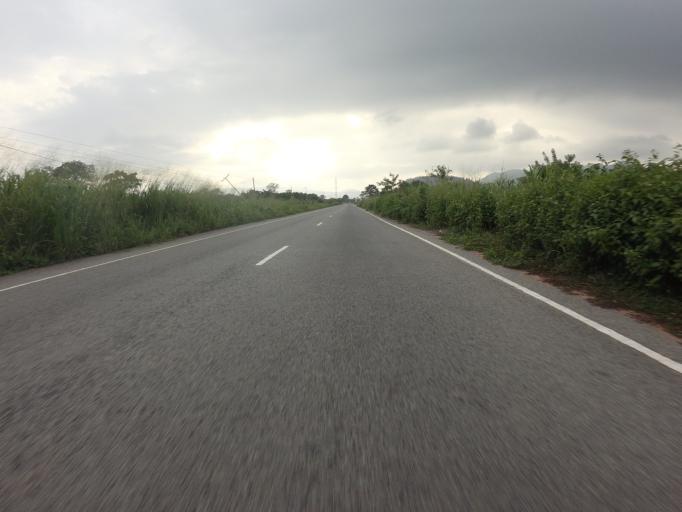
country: GH
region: Volta
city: Ho
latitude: 6.7803
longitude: 0.4673
